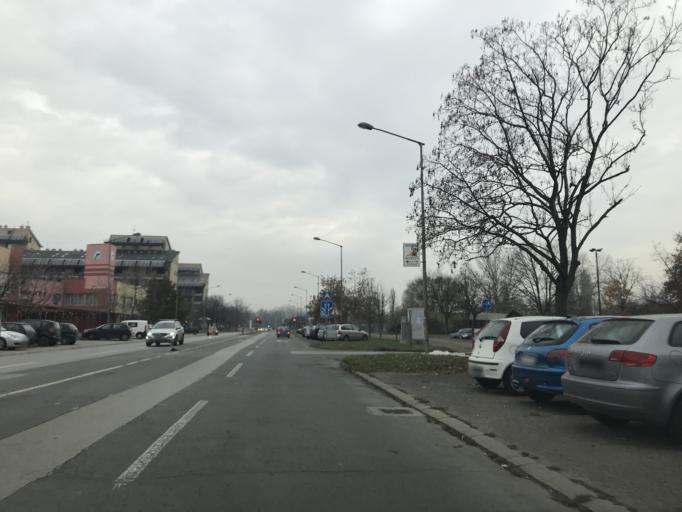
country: RS
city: Veternik
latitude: 45.2527
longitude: 19.7962
